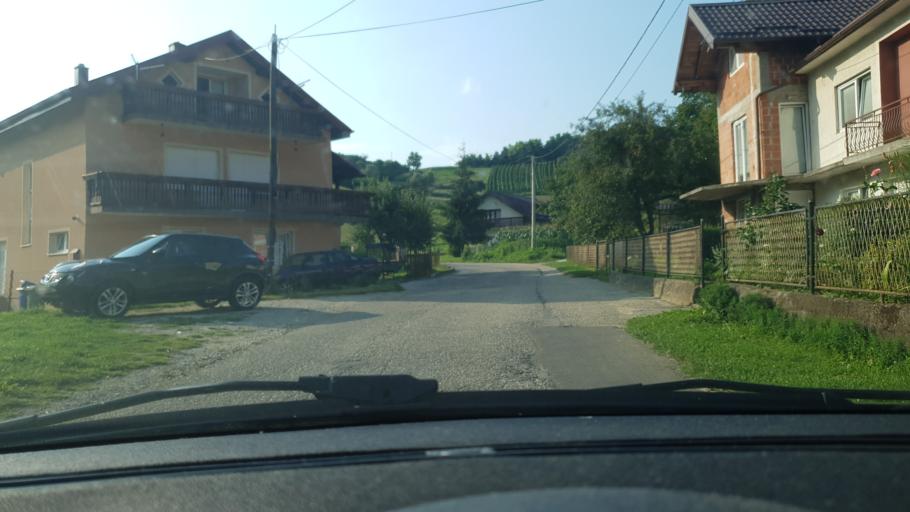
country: HR
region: Krapinsko-Zagorska
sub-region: Grad Krapina
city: Krapina
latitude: 46.1209
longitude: 15.9049
